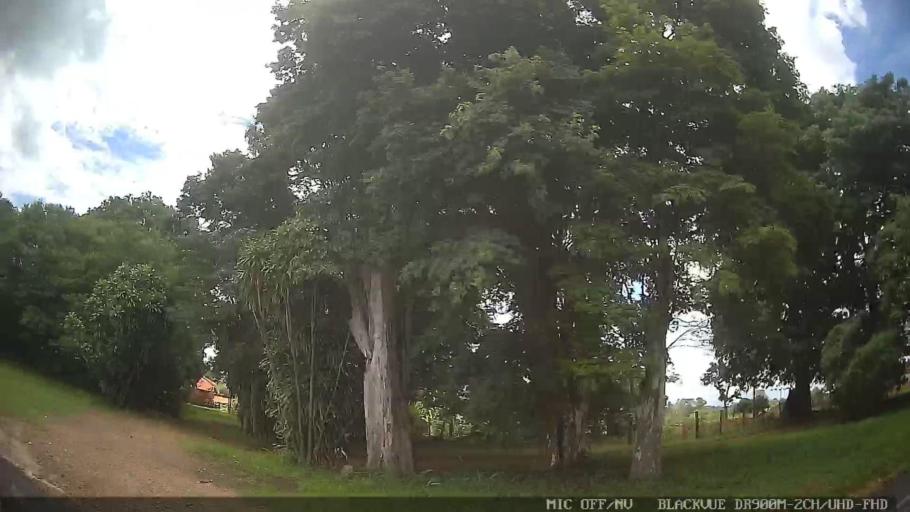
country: BR
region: Sao Paulo
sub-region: Laranjal Paulista
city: Laranjal Paulista
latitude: -23.0400
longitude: -47.9012
